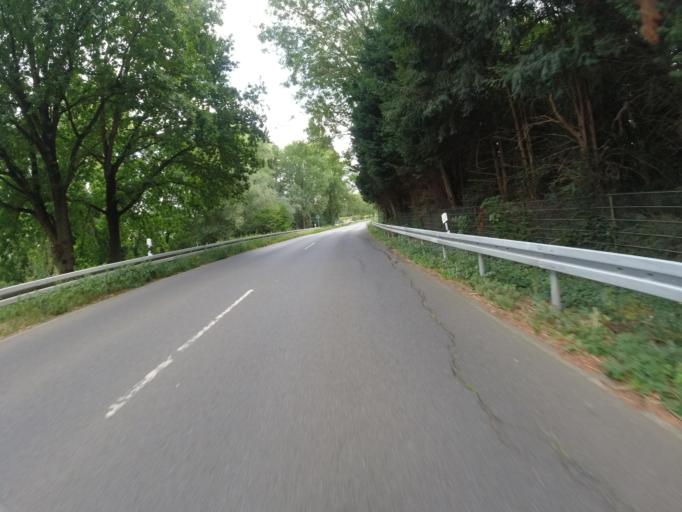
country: DE
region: North Rhine-Westphalia
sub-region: Regierungsbezirk Dusseldorf
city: Krefeld
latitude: 51.4040
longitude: 6.5618
